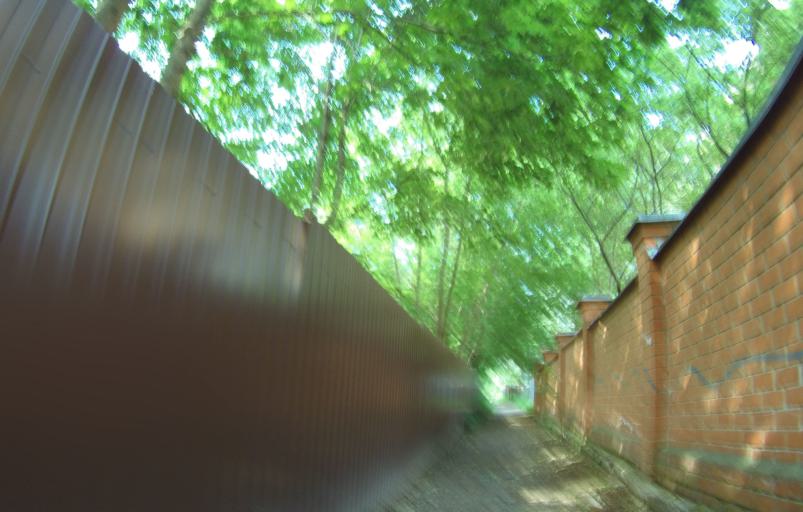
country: RU
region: Moskovskaya
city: Kraskovo
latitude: 55.6432
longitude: 37.9832
